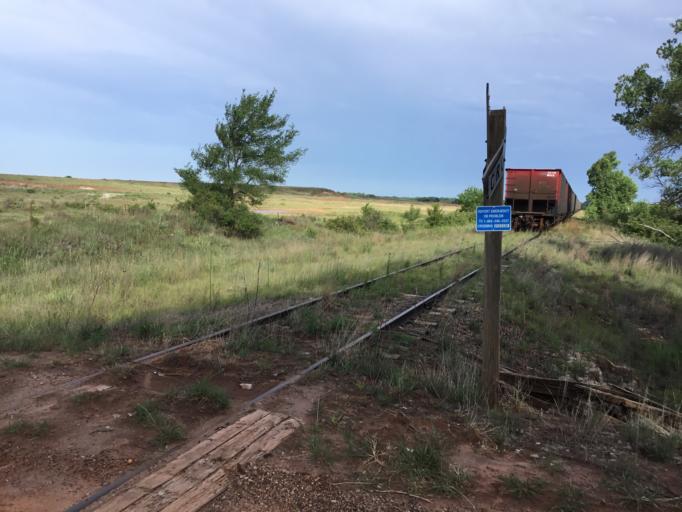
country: US
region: Kansas
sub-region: Kingman County
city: Kingman
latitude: 37.6189
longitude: -97.9724
